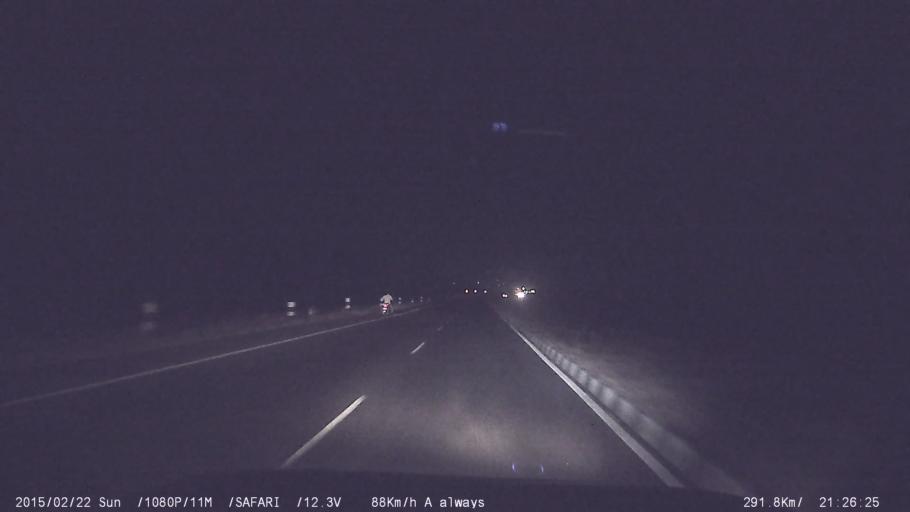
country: IN
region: Tamil Nadu
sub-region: Karur
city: Karur
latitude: 10.9048
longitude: 78.0359
